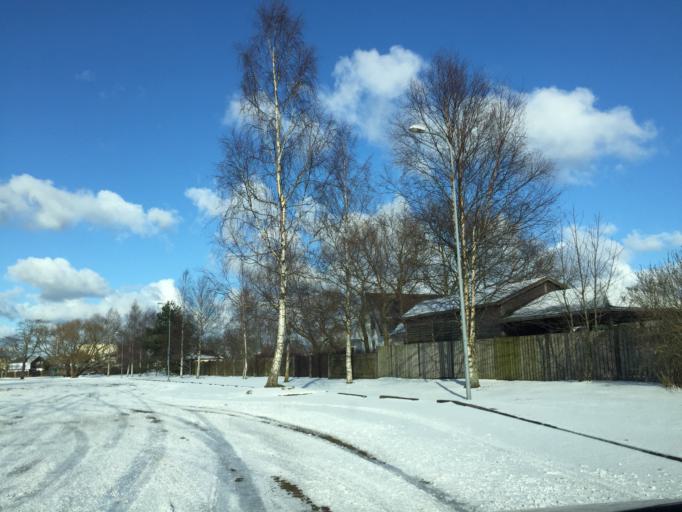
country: LV
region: Ventspils
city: Ventspils
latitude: 57.3893
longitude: 21.5374
